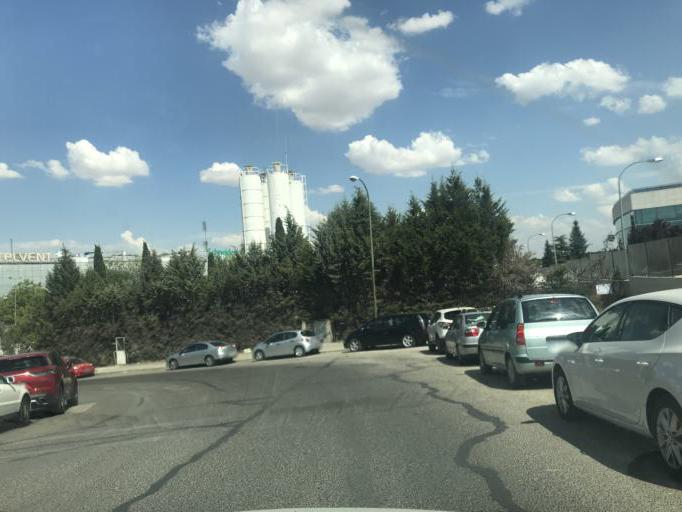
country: ES
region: Madrid
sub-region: Provincia de Madrid
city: Alcobendas
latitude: 40.5362
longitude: -3.6510
